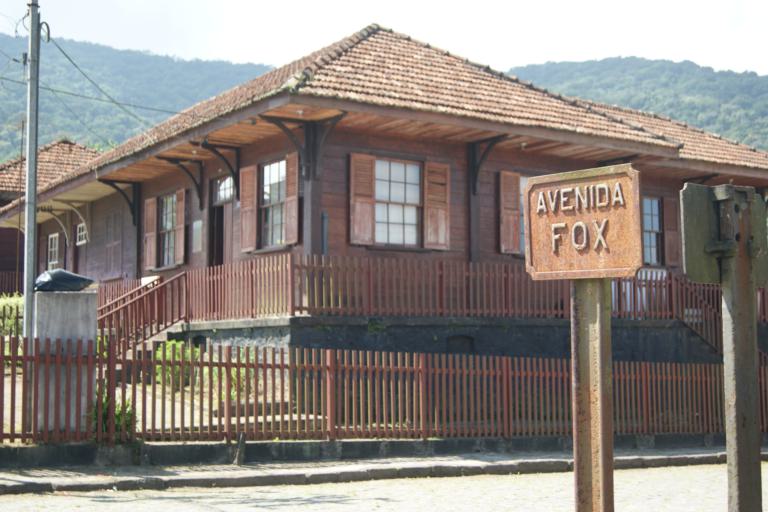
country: BR
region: Sao Paulo
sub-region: Rio Grande Da Serra
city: Rio Grande da Serra
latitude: -23.7767
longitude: -46.3003
